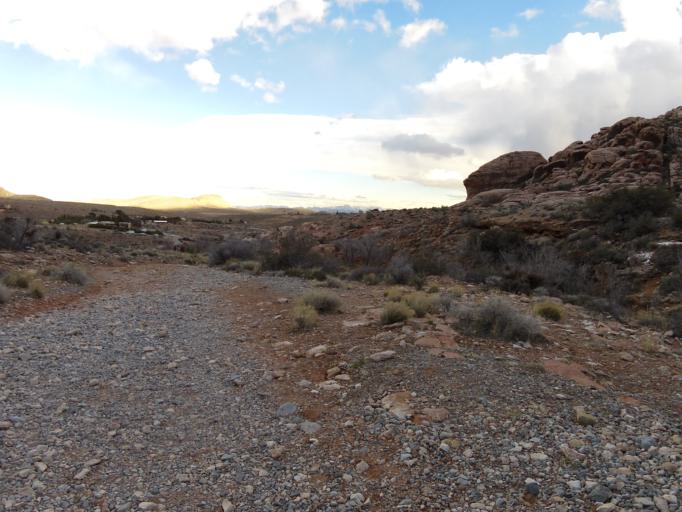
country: US
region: Nevada
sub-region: Clark County
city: Summerlin South
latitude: 36.1506
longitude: -115.4244
